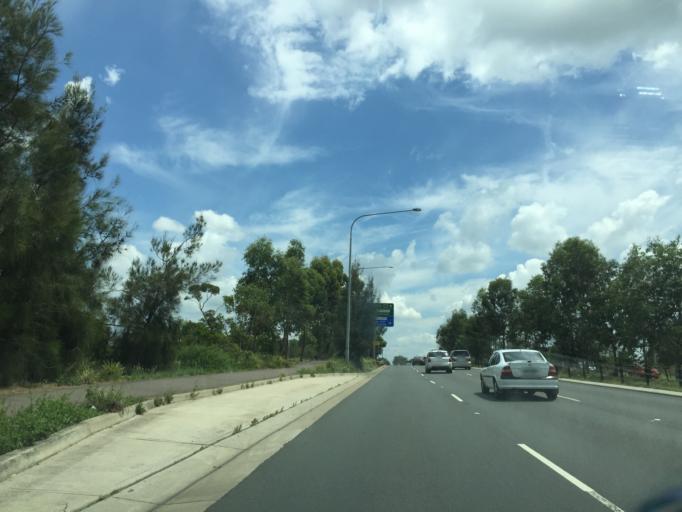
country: AU
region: New South Wales
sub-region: Blacktown
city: Rouse Hill
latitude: -33.6931
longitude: 150.9244
